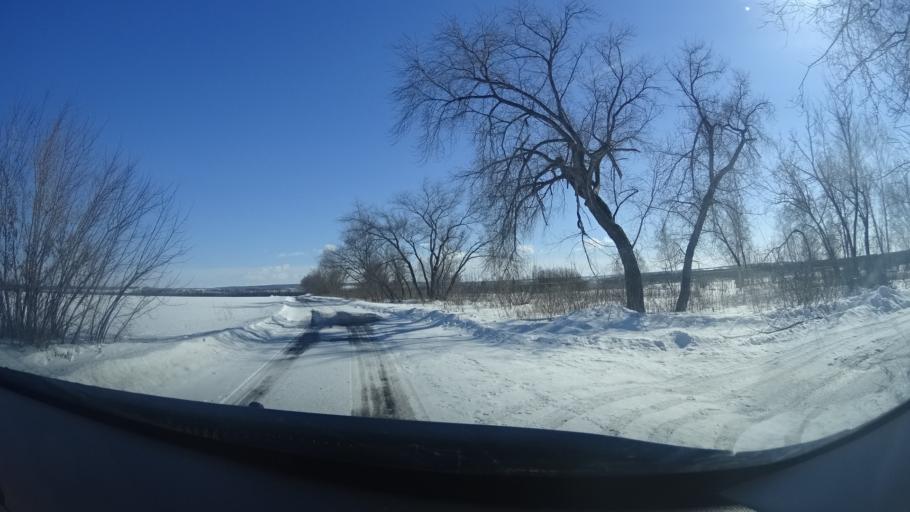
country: RU
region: Bashkortostan
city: Chishmy
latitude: 54.5834
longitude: 55.4153
